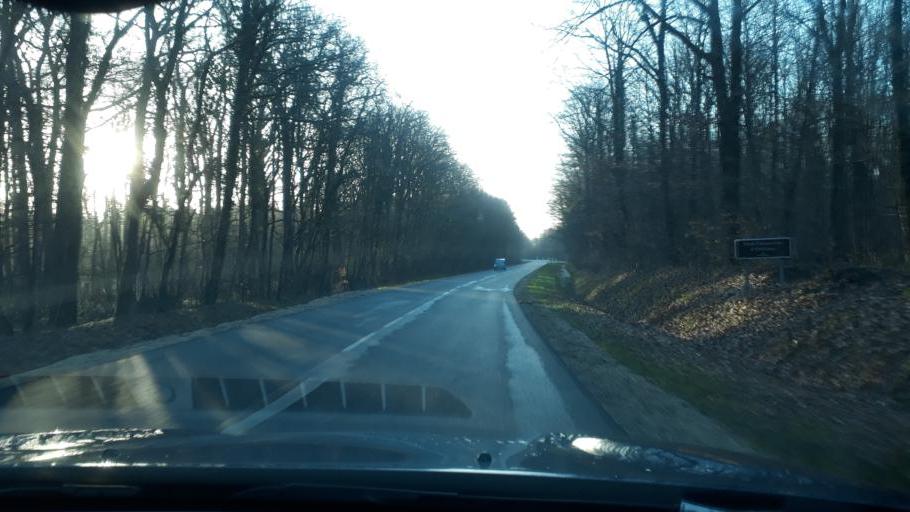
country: FR
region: Centre
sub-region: Departement du Loiret
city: Neuville-aux-Bois
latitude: 48.0427
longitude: 2.0628
